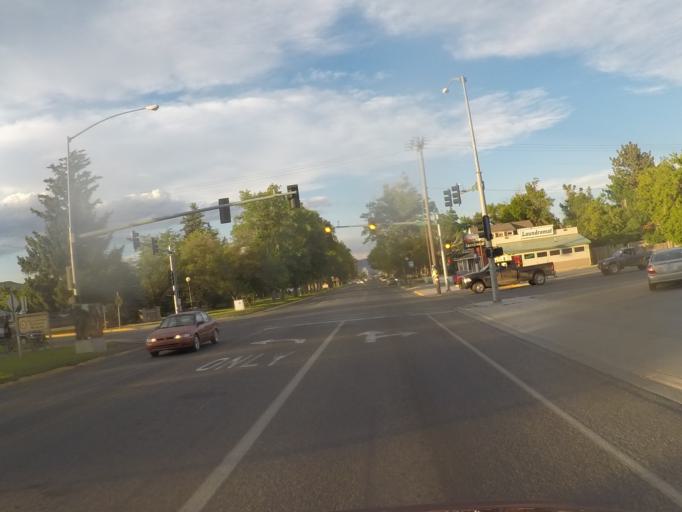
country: US
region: Montana
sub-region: Park County
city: Livingston
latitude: 45.6597
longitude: -110.5661
